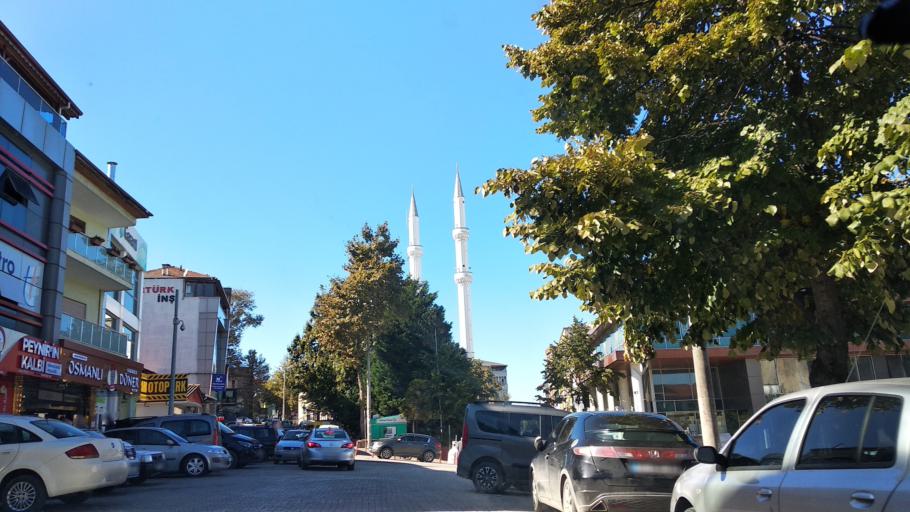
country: TR
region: Sakarya
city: Karasu
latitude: 41.0931
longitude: 30.6917
